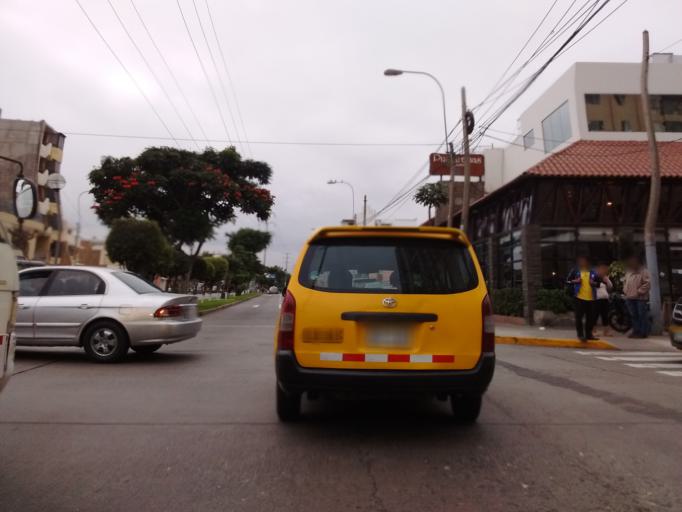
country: PE
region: Callao
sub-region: Callao
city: Callao
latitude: -12.0741
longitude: -77.0920
